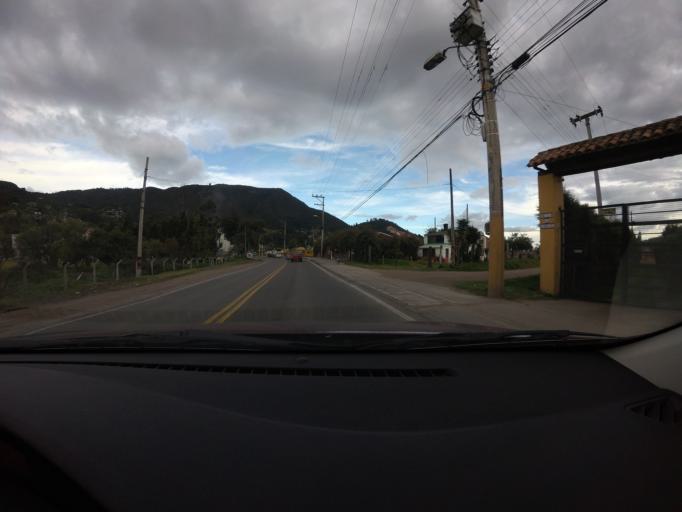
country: CO
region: Cundinamarca
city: Sopo
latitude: 4.9164
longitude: -73.9449
